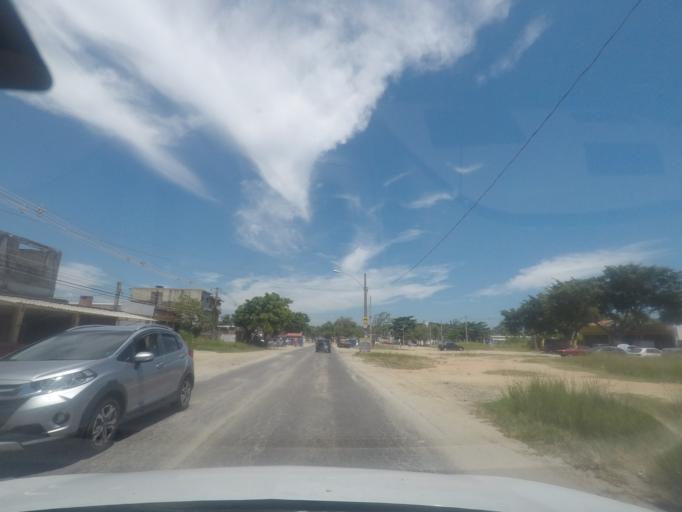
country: BR
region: Rio de Janeiro
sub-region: Itaguai
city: Itaguai
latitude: -22.9832
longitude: -43.6614
